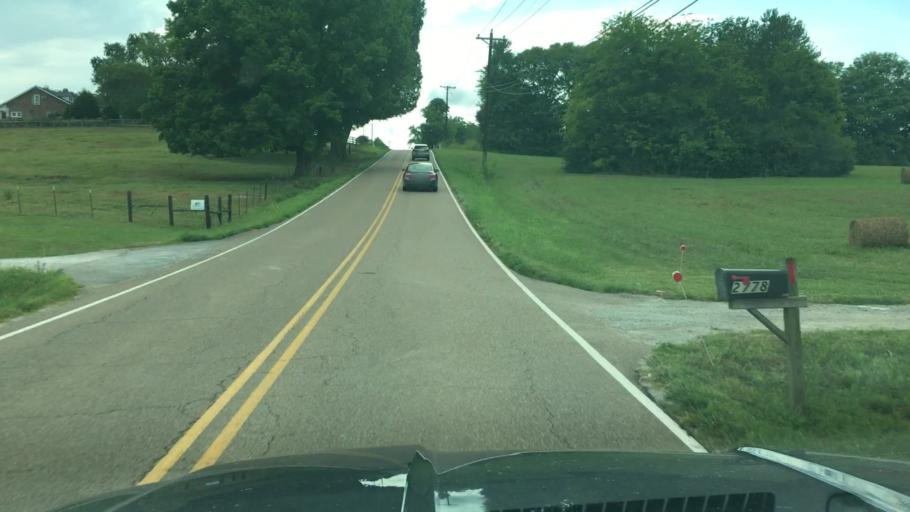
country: US
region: Tennessee
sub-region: Williamson County
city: Thompson's Station
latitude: 35.8083
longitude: -86.8592
